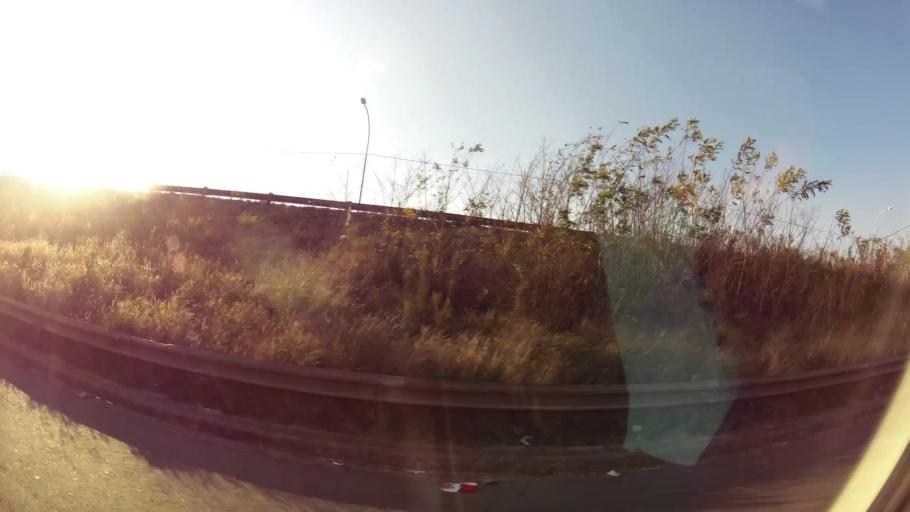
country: ZA
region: Gauteng
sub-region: Ekurhuleni Metropolitan Municipality
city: Germiston
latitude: -26.2102
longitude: 28.1179
